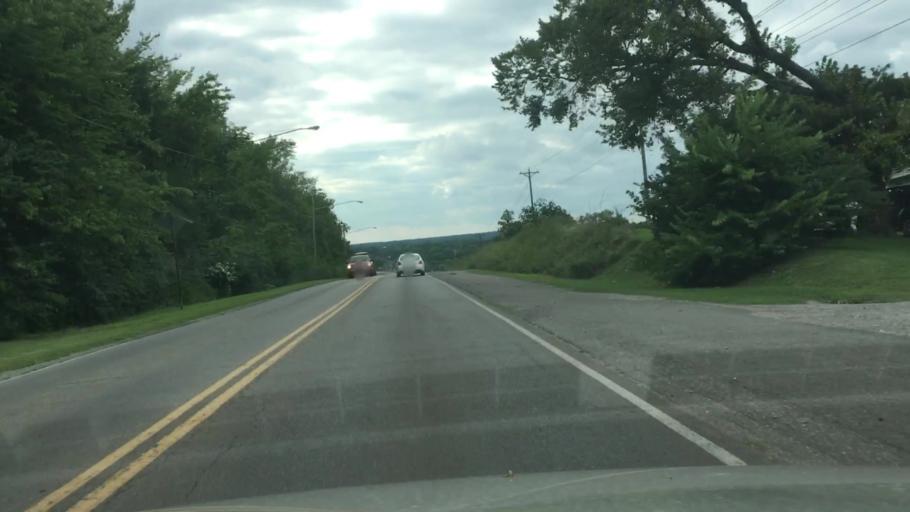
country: US
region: Oklahoma
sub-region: Cherokee County
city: Tahlequah
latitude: 35.9179
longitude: -94.9933
